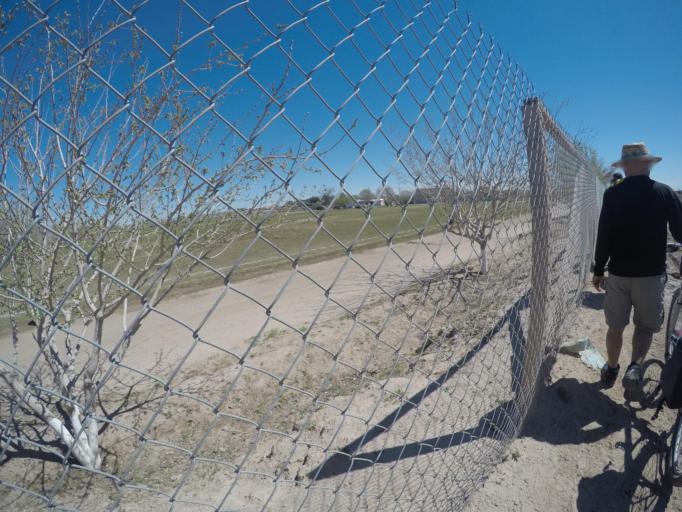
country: US
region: Texas
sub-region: El Paso County
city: Socorro Mission Number 1 Colonia
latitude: 31.6099
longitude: -106.3136
